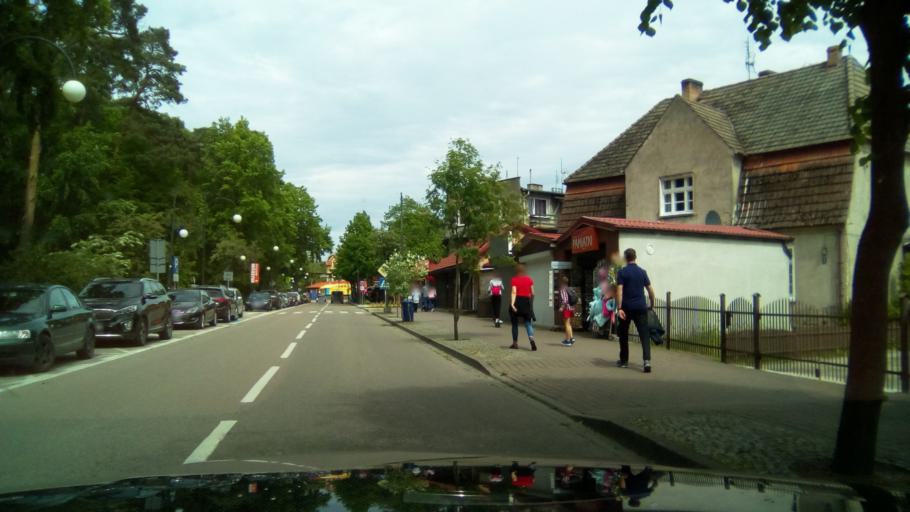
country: PL
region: Pomeranian Voivodeship
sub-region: Powiat leborski
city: Leba
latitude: 54.7635
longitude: 17.5566
